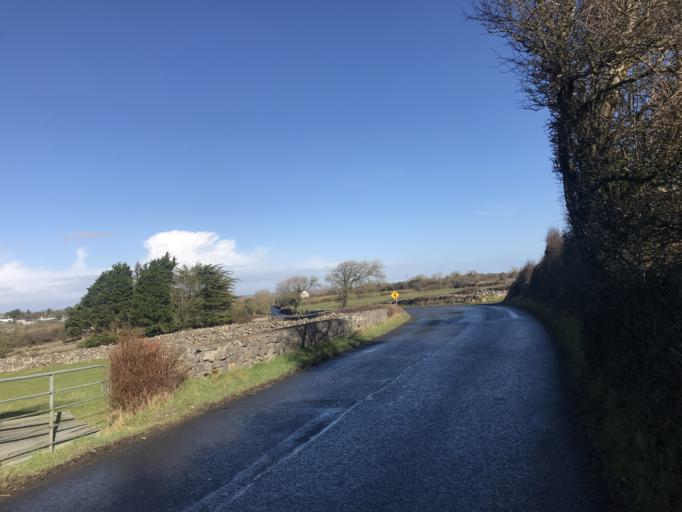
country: IE
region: Connaught
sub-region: County Galway
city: Gaillimh
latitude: 53.3063
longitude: -9.0193
